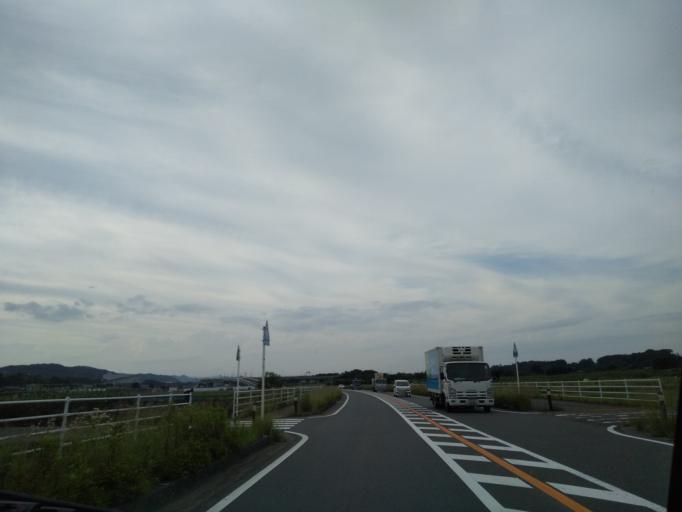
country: JP
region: Kanagawa
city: Zama
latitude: 35.4777
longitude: 139.3577
